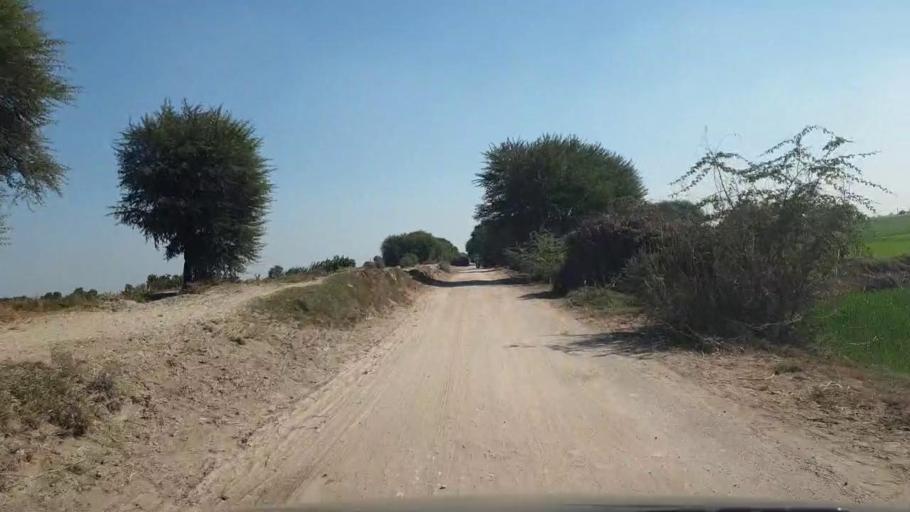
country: PK
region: Sindh
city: Shahpur Chakar
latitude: 26.1423
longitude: 68.6534
